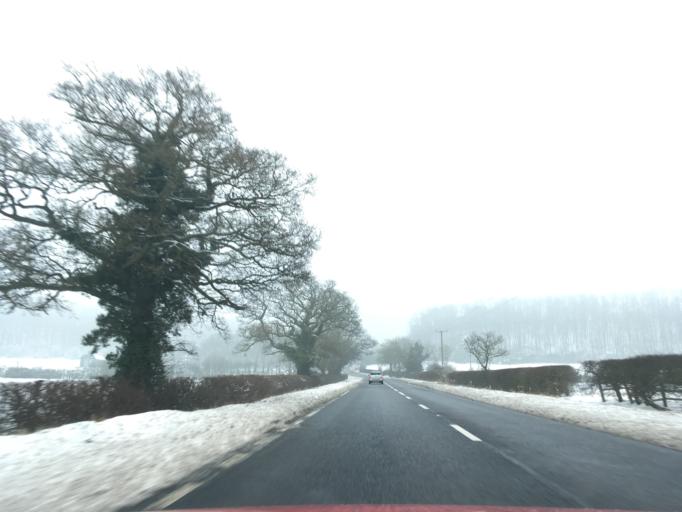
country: GB
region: England
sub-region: Warwickshire
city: Alcester
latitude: 52.2051
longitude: -1.8093
